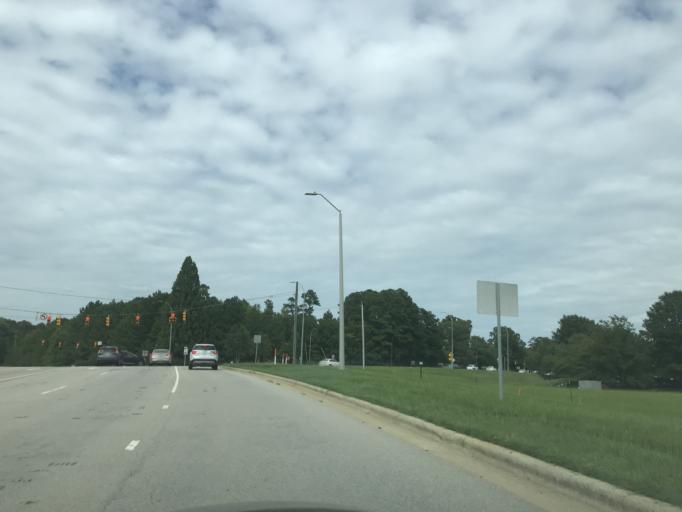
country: US
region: North Carolina
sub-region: Wake County
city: Cary
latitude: 35.7357
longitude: -78.7878
